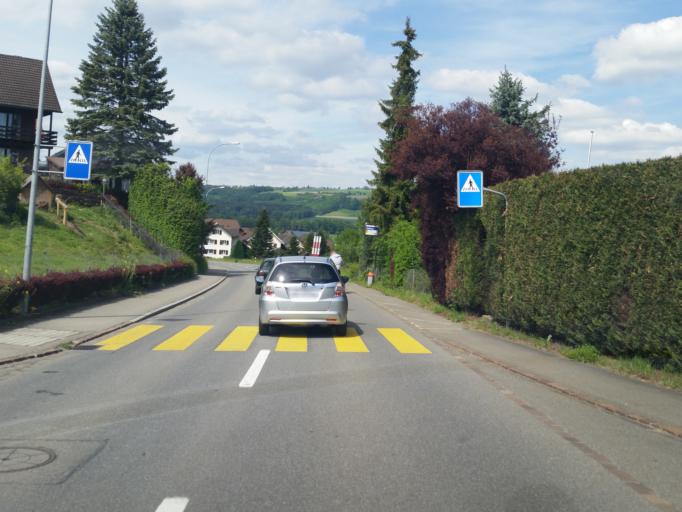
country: CH
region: Aargau
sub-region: Bezirk Bremgarten
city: Unterlunkhofen
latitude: 47.3111
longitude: 8.3605
